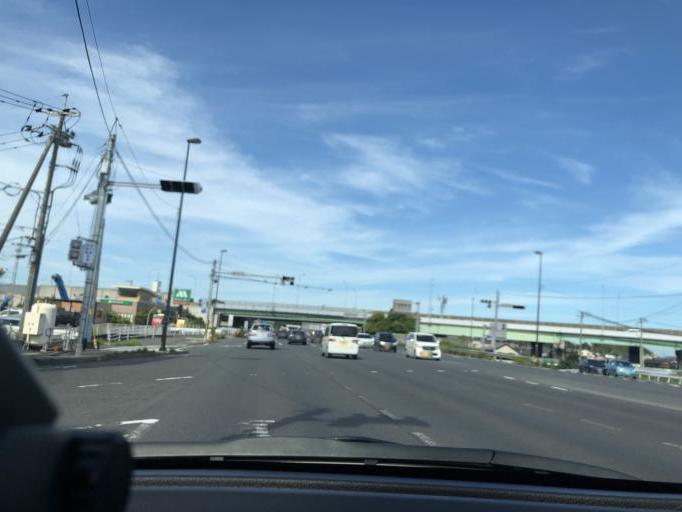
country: JP
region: Okayama
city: Kurashiki
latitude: 34.5984
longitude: 133.8100
